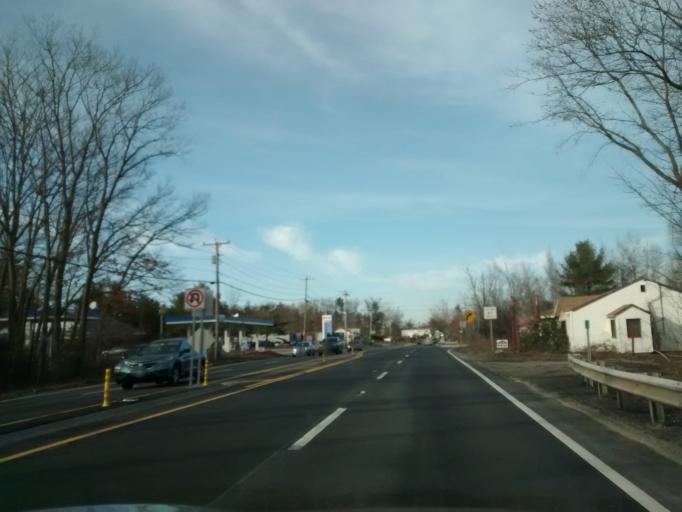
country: US
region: Massachusetts
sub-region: Worcester County
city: Oxford
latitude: 42.1615
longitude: -71.8999
